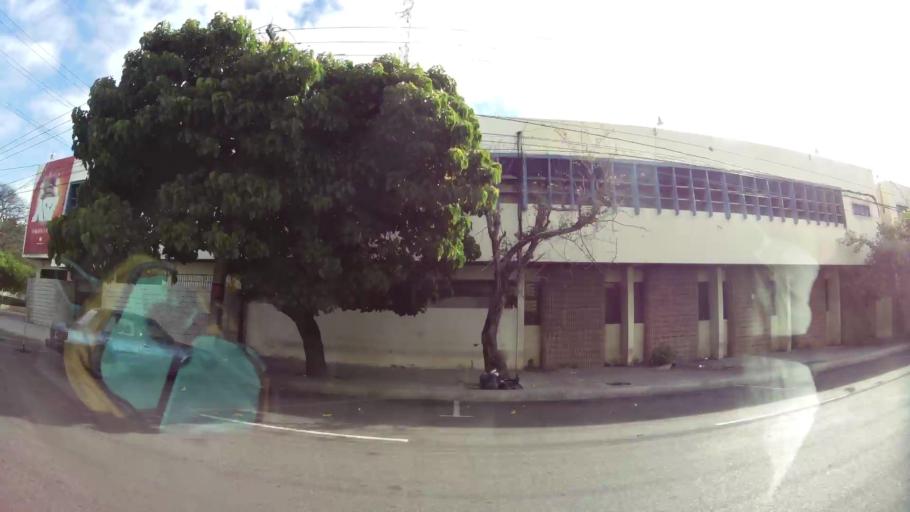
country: DO
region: Nacional
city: La Julia
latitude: 18.4515
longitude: -69.9262
